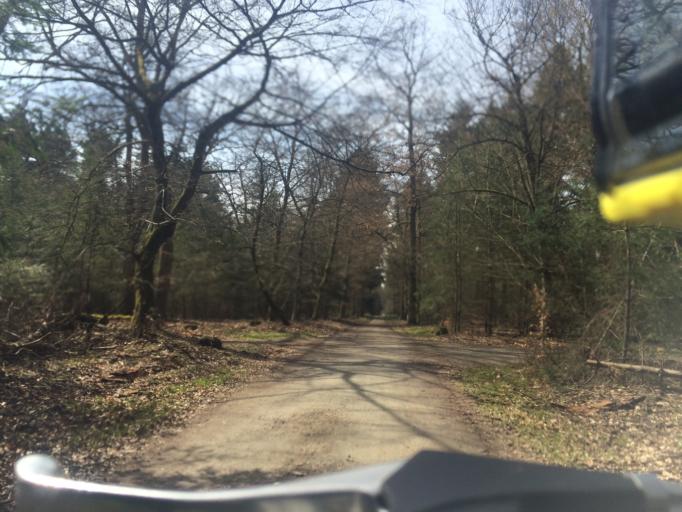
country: DE
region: Hesse
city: Morfelden-Walldorf
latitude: 50.0026
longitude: 8.5487
